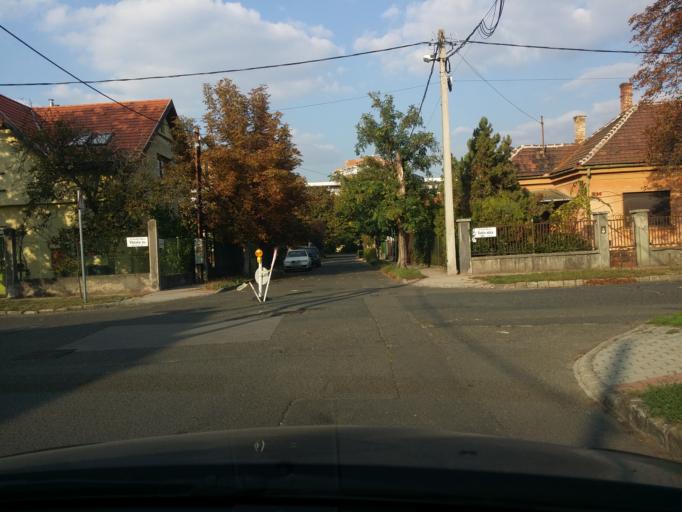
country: HU
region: Budapest
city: Budapest XV. keruelet
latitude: 47.5773
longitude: 19.1036
